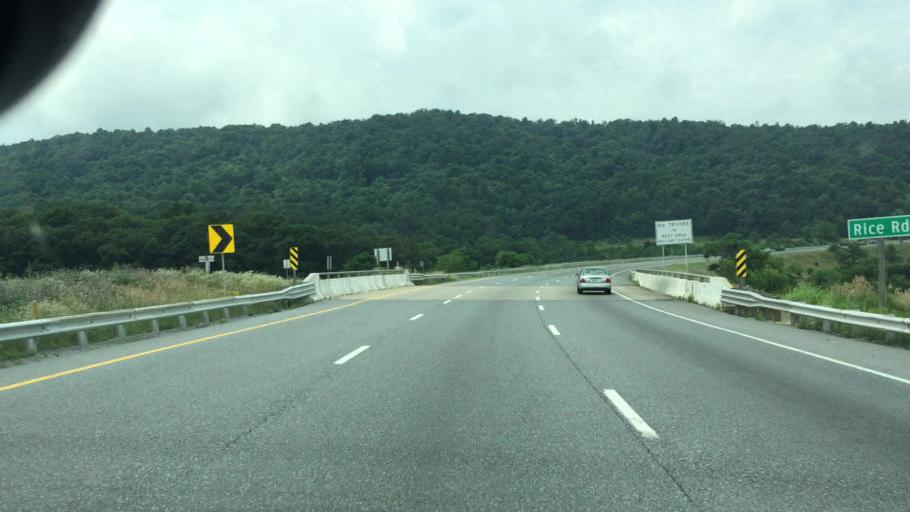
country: US
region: Maryland
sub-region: Washington County
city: Hancock
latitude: 39.7102
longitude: -78.2752
